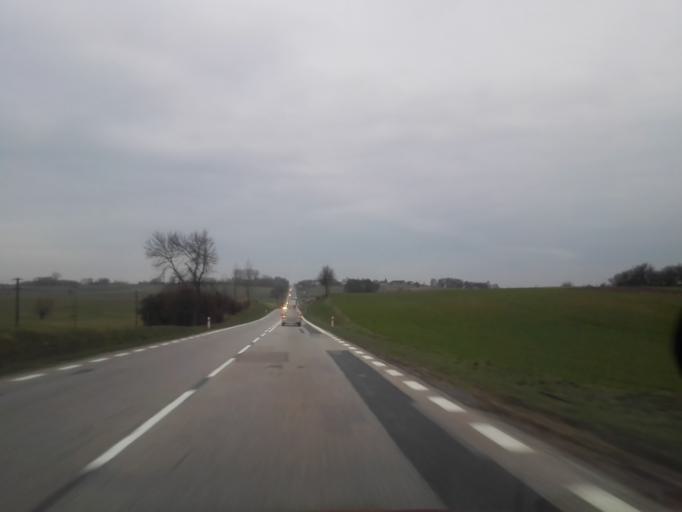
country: PL
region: Podlasie
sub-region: Powiat lomzynski
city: Piatnica
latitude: 53.2404
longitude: 22.1161
